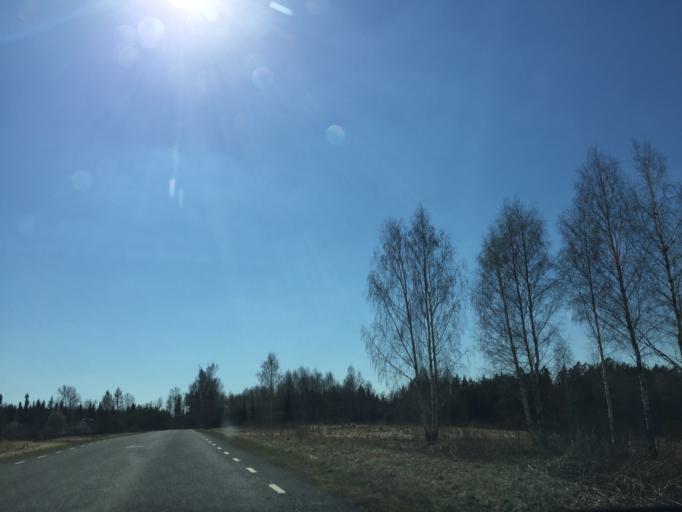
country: EE
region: Viljandimaa
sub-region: Viljandi linn
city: Viljandi
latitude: 58.2936
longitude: 25.5948
